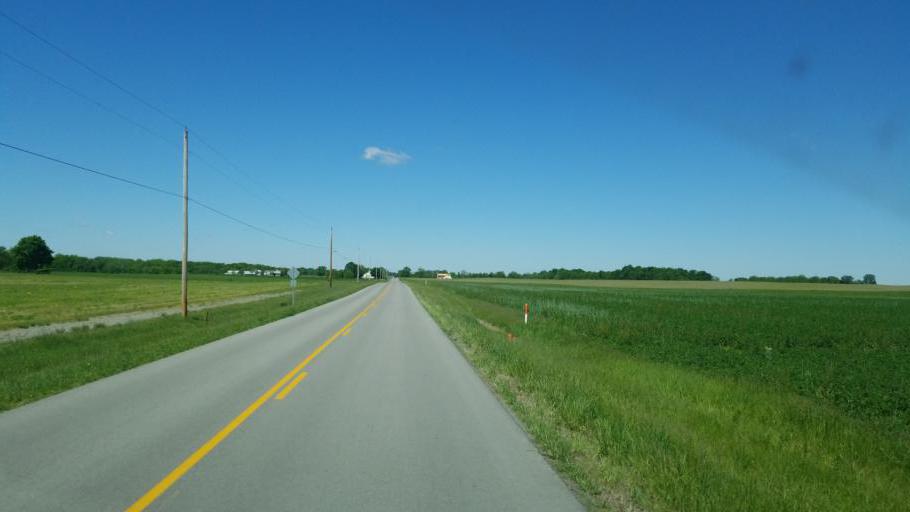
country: US
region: Ohio
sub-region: Logan County
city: Russells Point
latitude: 40.4249
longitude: -83.8595
